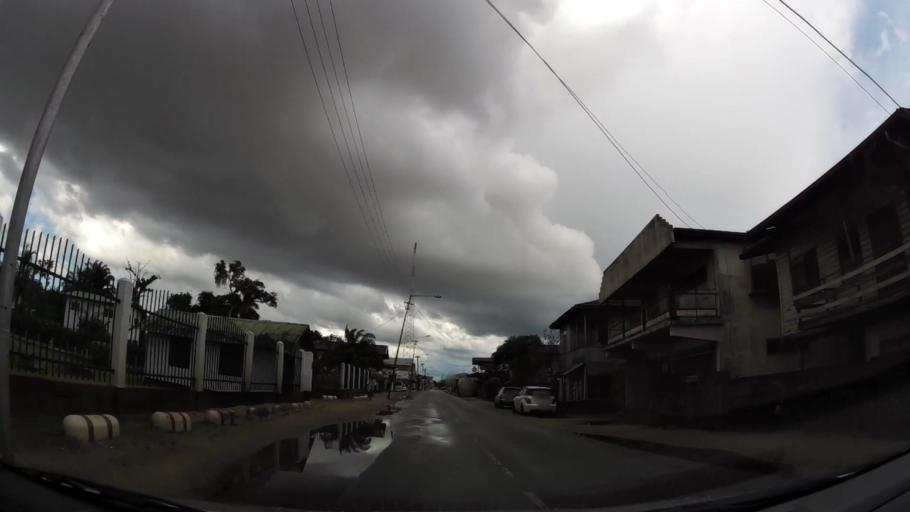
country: SR
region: Paramaribo
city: Paramaribo
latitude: 5.8360
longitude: -55.1708
